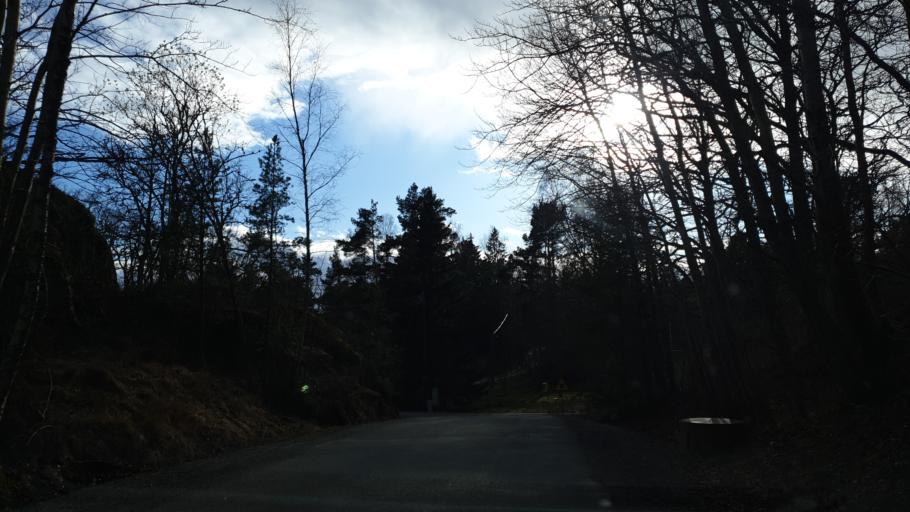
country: SE
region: Stockholm
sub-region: Varmdo Kommun
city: Holo
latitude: 59.3704
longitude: 18.6709
